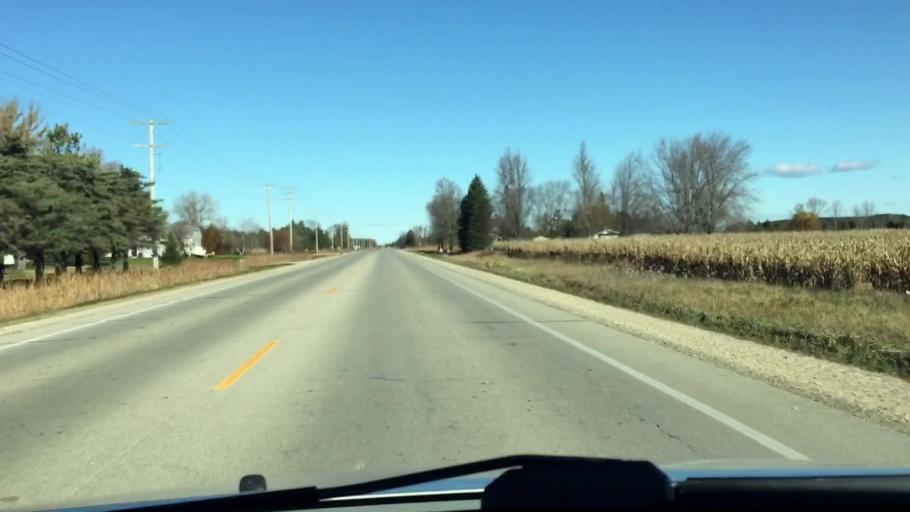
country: US
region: Wisconsin
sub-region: Brown County
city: Pulaski
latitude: 44.6893
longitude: -88.2429
